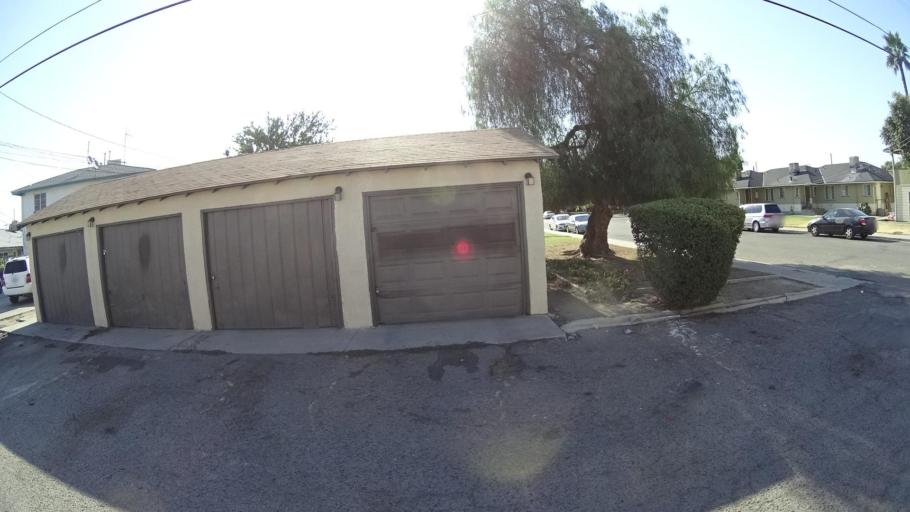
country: US
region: California
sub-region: Fresno County
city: Fresno
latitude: 36.7662
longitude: -119.7701
